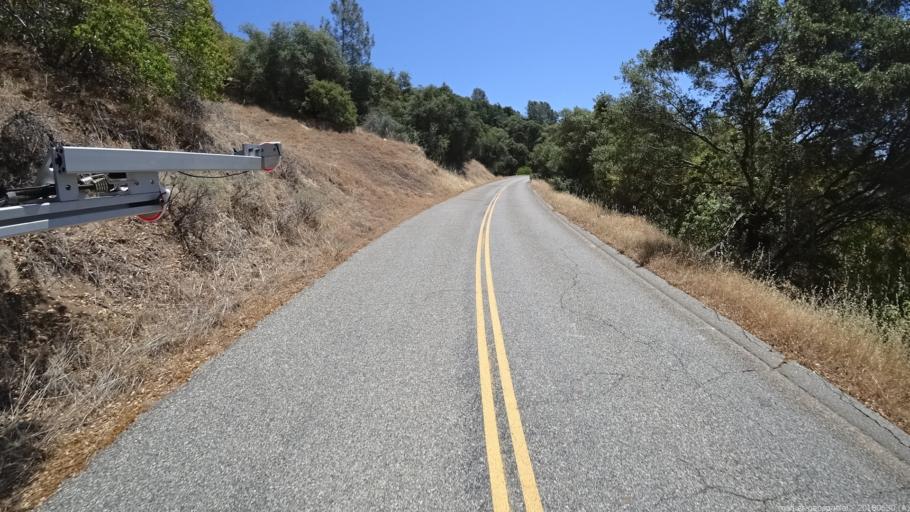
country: US
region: California
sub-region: Fresno County
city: Auberry
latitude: 37.1837
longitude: -119.4532
